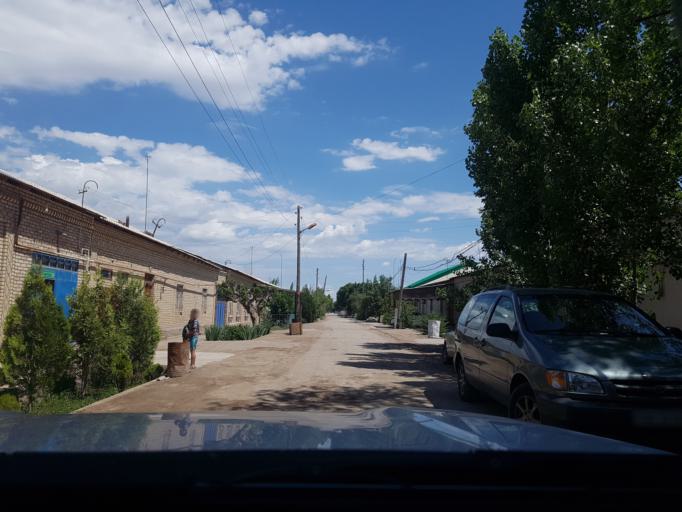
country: TM
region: Dasoguz
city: Dasoguz
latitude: 41.8355
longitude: 60.1338
